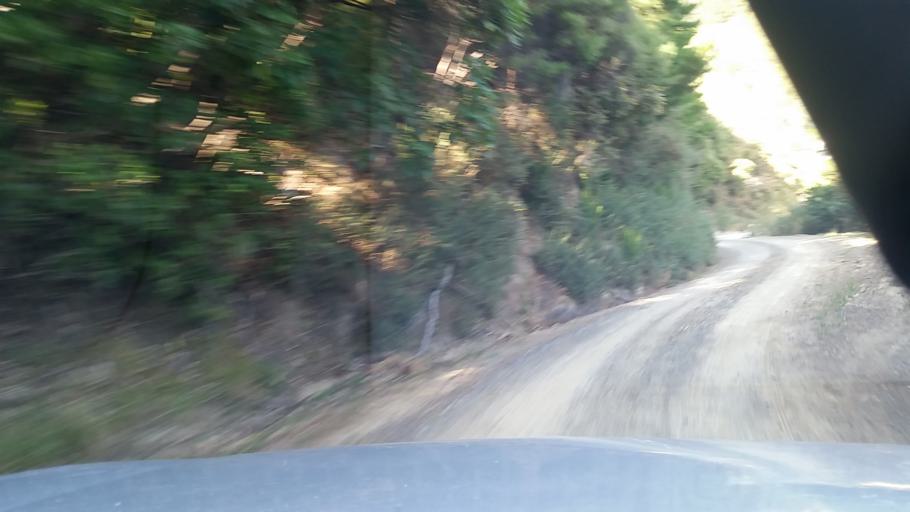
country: NZ
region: Marlborough
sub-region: Marlborough District
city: Picton
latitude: -41.3024
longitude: 174.1782
